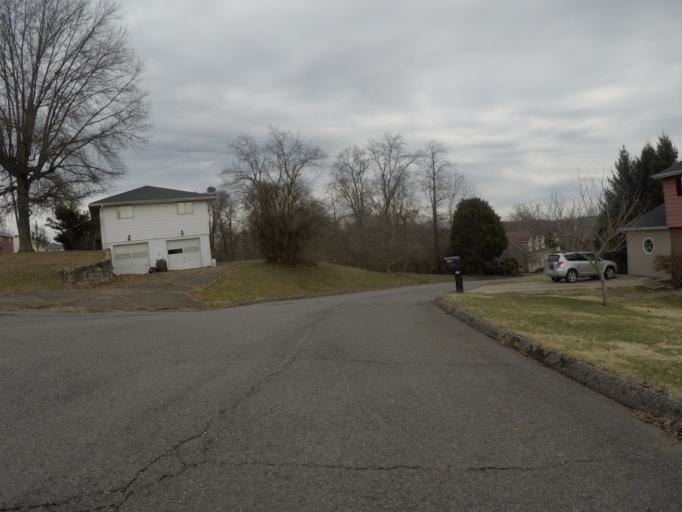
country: US
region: West Virginia
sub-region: Cabell County
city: Pea Ridge
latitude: 38.3951
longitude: -82.3804
